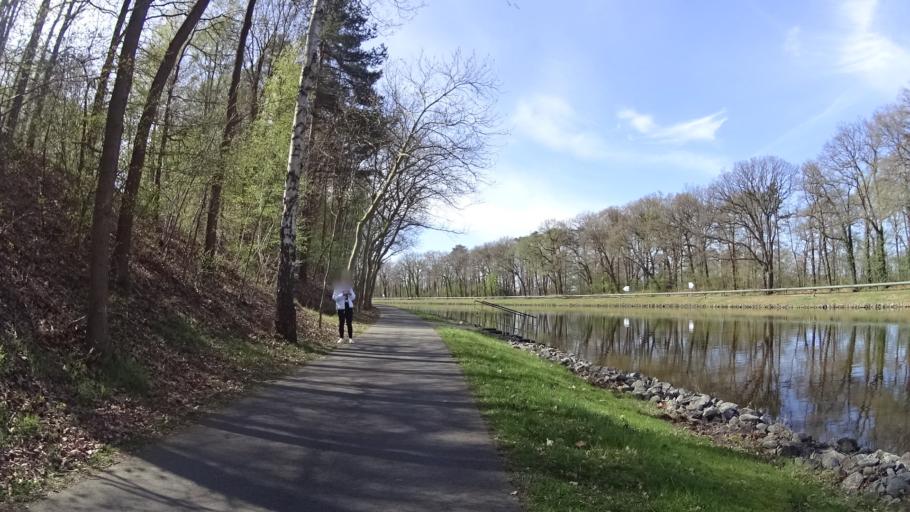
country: DE
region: Lower Saxony
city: Lingen
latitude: 52.5556
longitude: 7.2959
